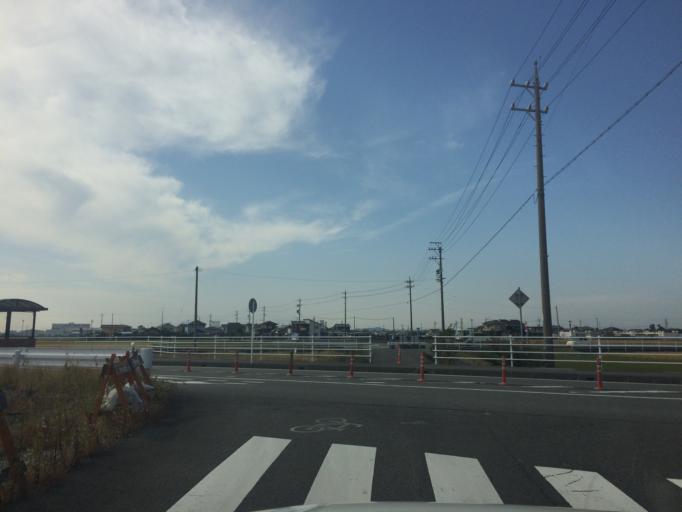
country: JP
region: Shizuoka
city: Yaizu
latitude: 34.8111
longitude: 138.3113
